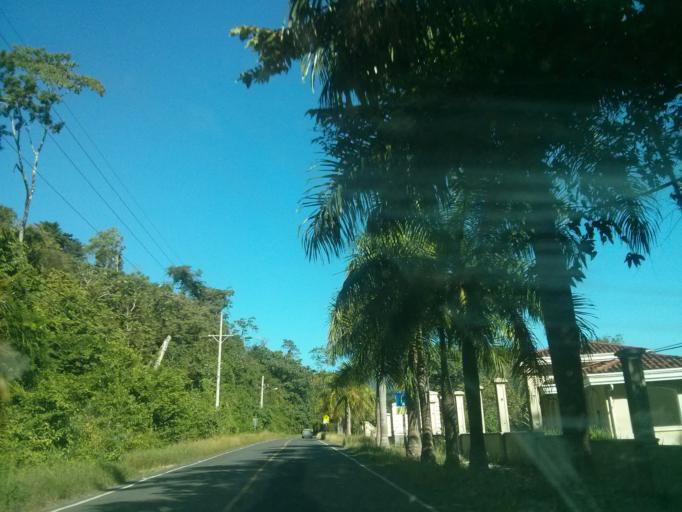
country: CR
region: Puntarenas
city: Paquera
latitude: 9.7159
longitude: -85.0182
